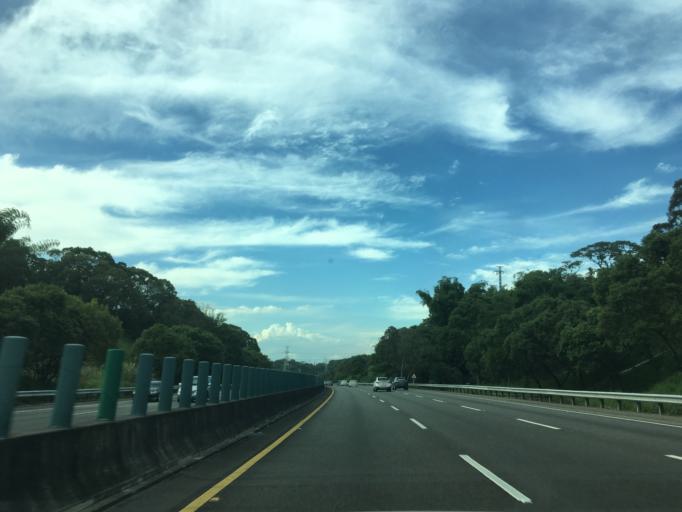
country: TW
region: Taiwan
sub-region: Chiayi
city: Jiayi Shi
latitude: 23.5496
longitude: 120.5046
